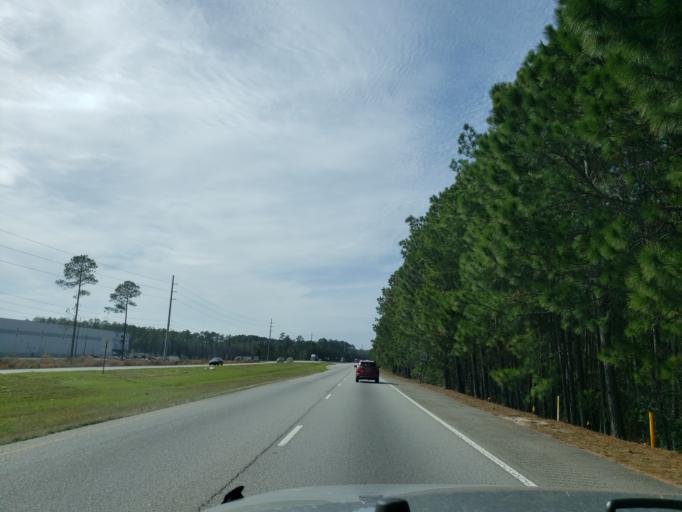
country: US
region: Georgia
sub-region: Chatham County
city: Pooler
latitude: 32.1672
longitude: -81.2237
